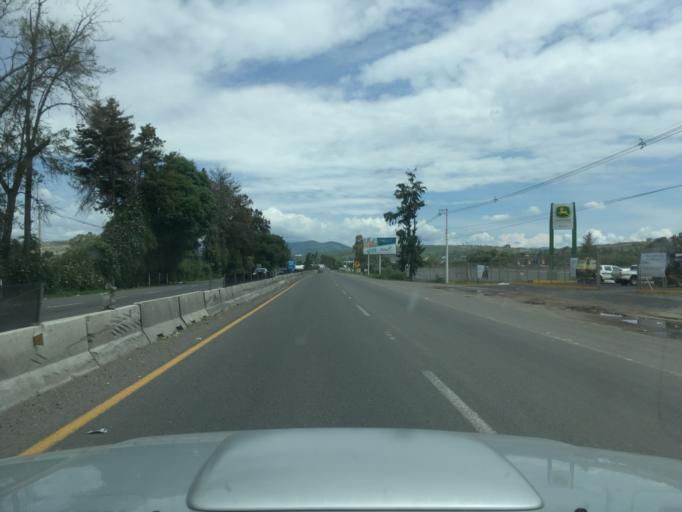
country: MX
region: Michoacan
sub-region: Tarimbaro
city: Conjunto Habitacional el Trebol
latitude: 19.7874
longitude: -101.1593
